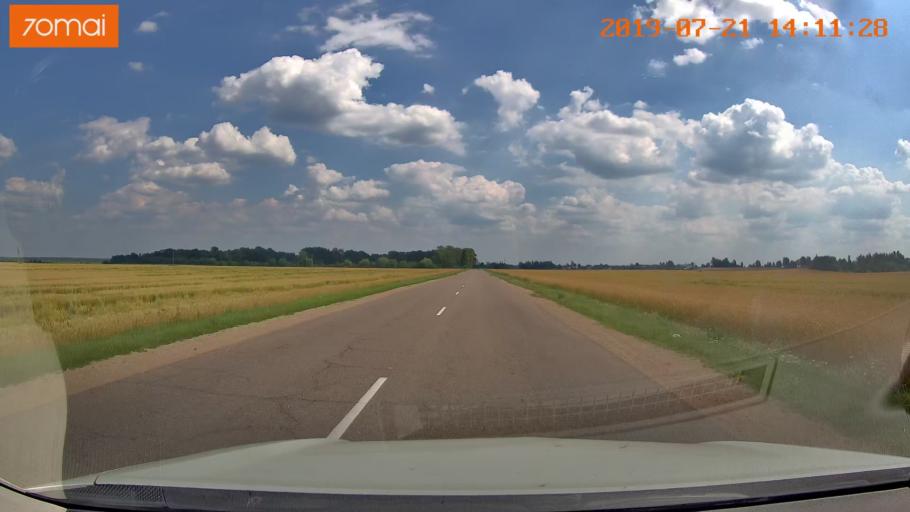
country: BY
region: Grodnenskaya
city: Karelichy
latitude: 53.6574
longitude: 26.1530
